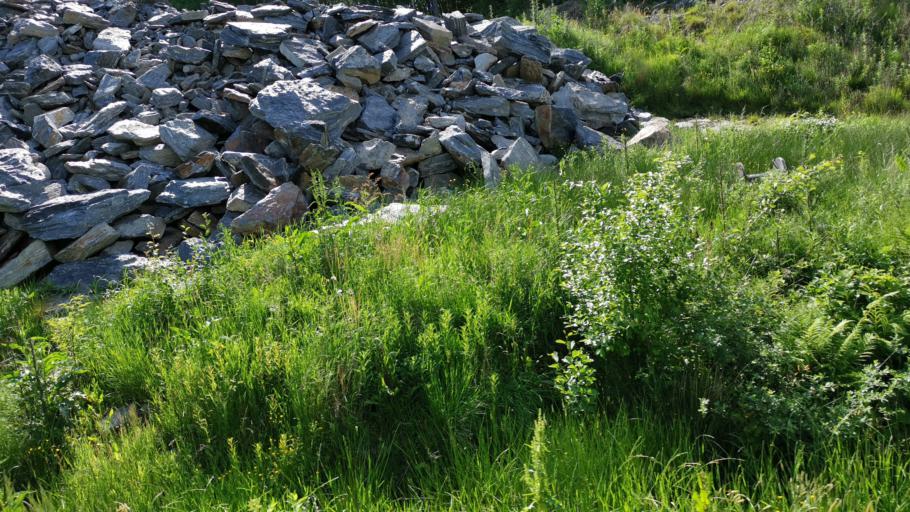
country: SE
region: Vaestra Goetaland
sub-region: Orust
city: Henan
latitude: 58.3184
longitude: 11.7202
